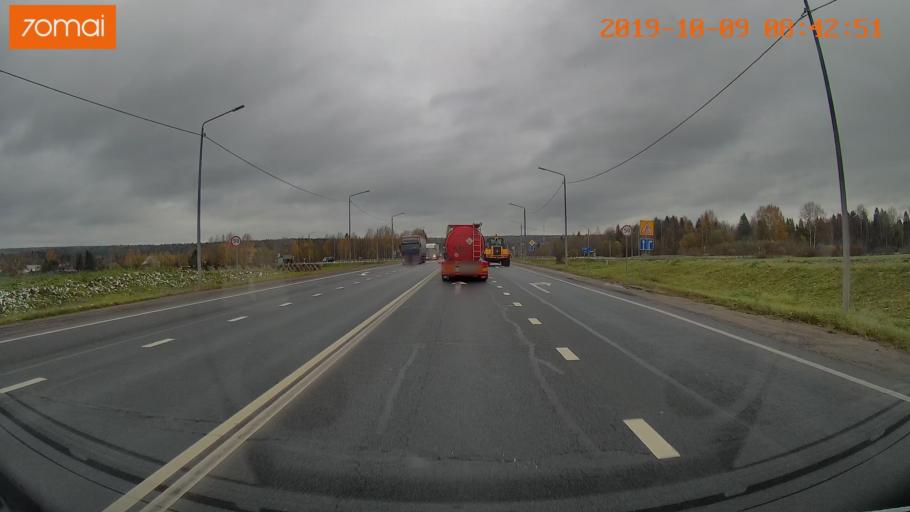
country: RU
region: Vologda
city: Gryazovets
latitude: 59.0191
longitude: 40.1168
